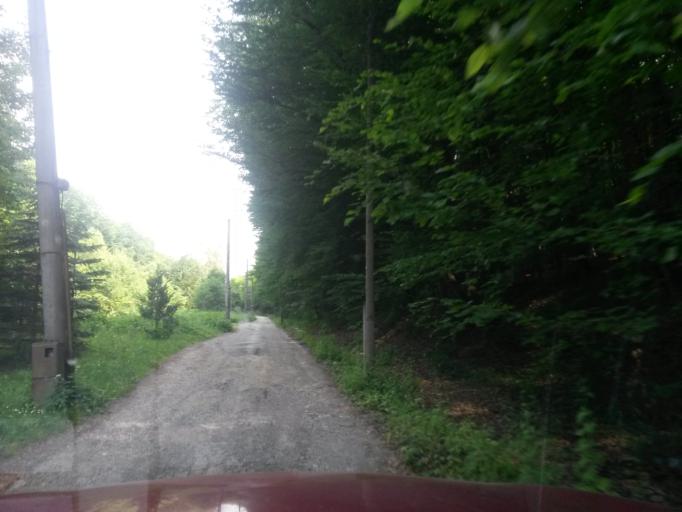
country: SK
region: Kosicky
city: Kosice
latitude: 48.7340
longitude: 21.1250
